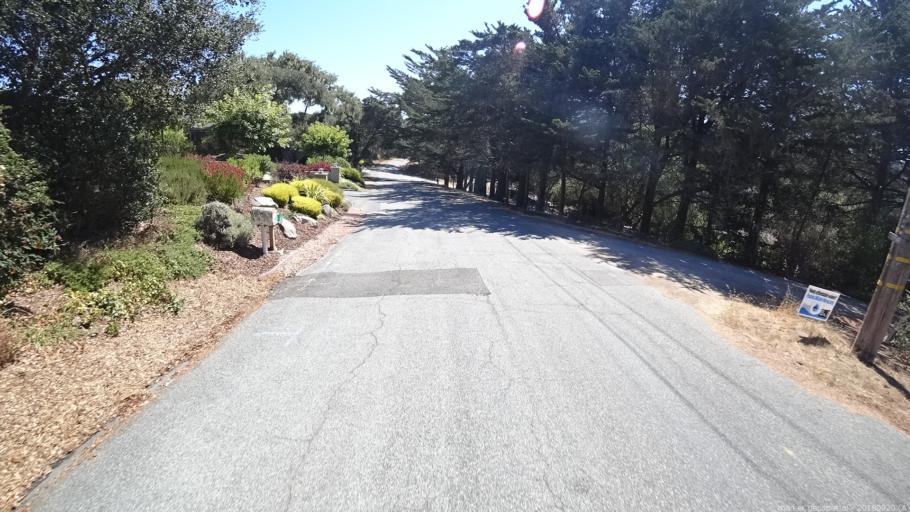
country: US
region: California
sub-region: Monterey County
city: Monterey
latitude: 36.5824
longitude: -121.8722
